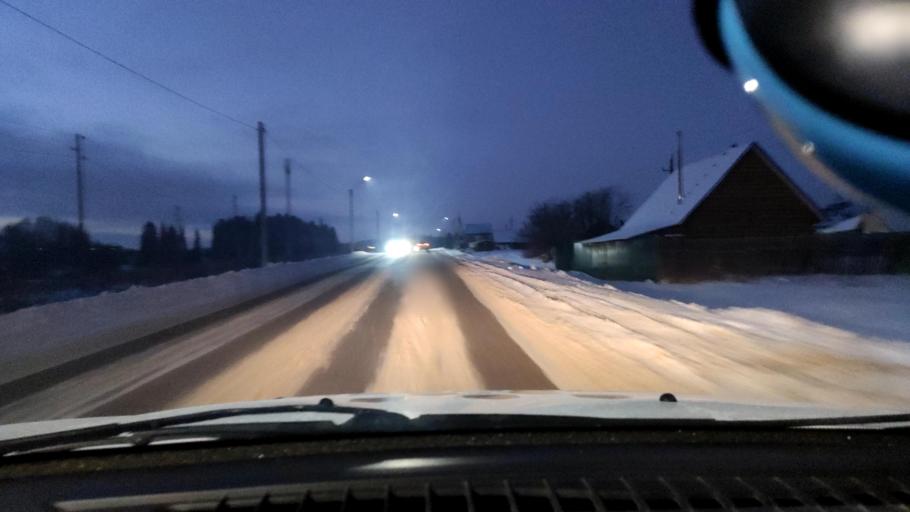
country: RU
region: Perm
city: Kultayevo
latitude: 57.9009
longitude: 55.9247
